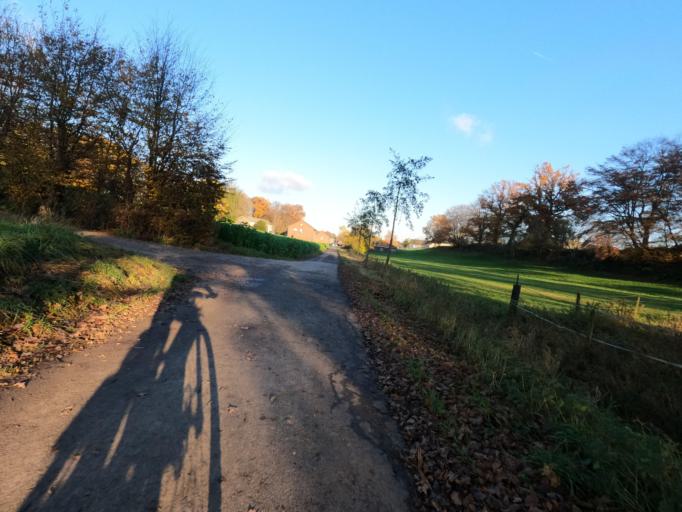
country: DE
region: North Rhine-Westphalia
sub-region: Regierungsbezirk Koln
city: Heinsberg
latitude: 51.0220
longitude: 6.1267
